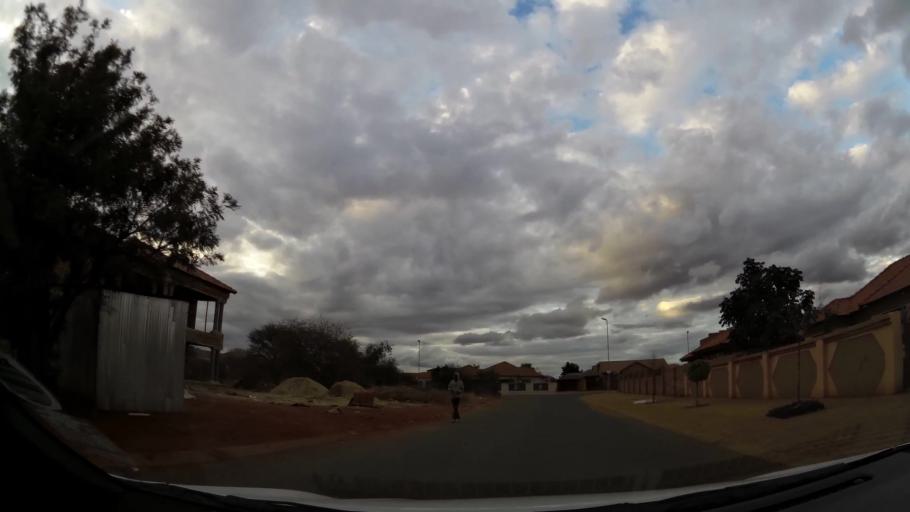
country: ZA
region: Limpopo
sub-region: Waterberg District Municipality
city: Mokopane
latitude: -24.2027
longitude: 28.9938
